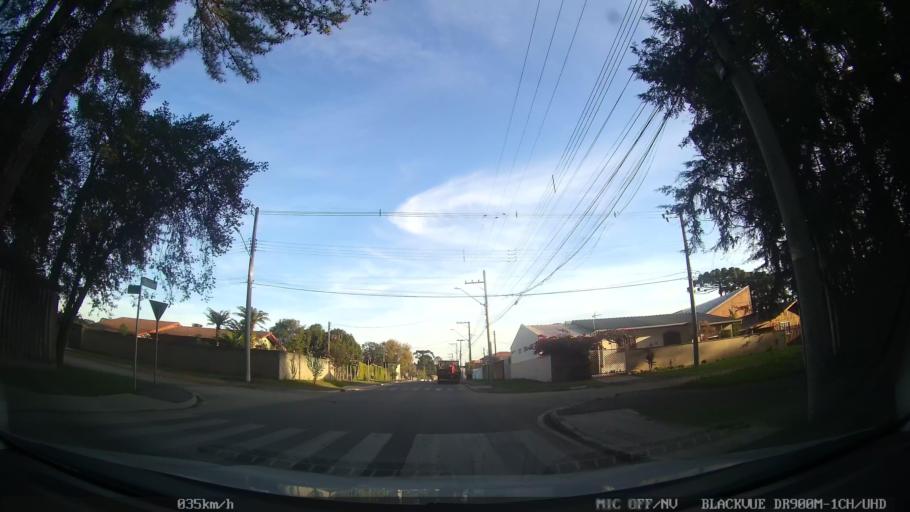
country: BR
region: Parana
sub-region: Pinhais
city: Pinhais
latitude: -25.4601
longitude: -49.1506
